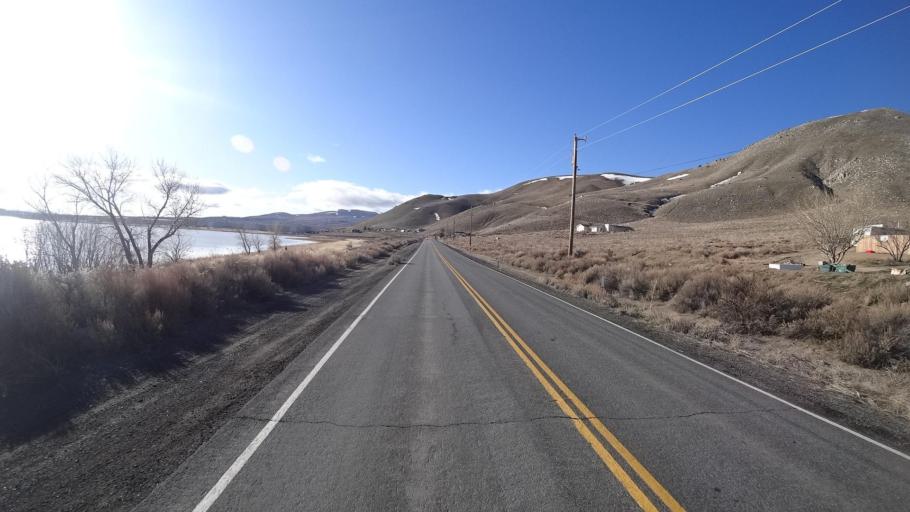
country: US
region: Nevada
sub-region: Washoe County
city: Cold Springs
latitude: 39.6442
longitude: -119.9260
